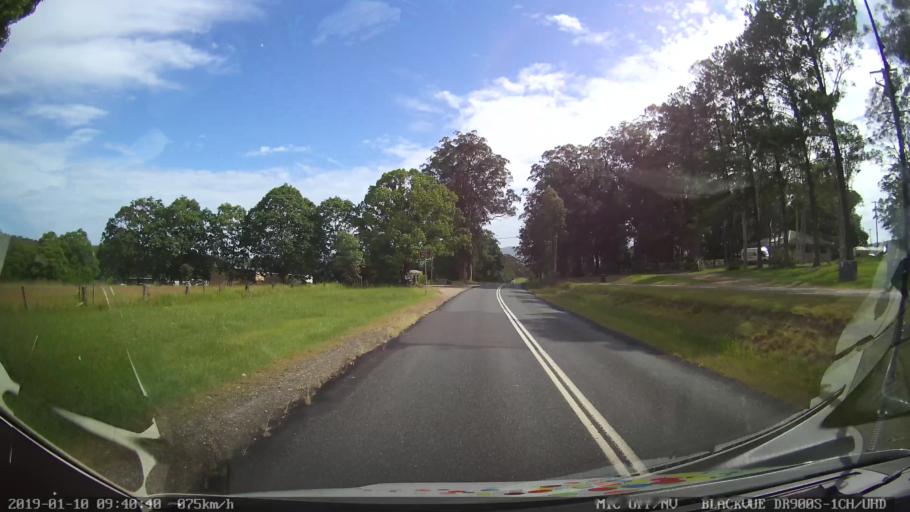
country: AU
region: New South Wales
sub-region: Coffs Harbour
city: Nana Glen
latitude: -30.1490
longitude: 153.0050
